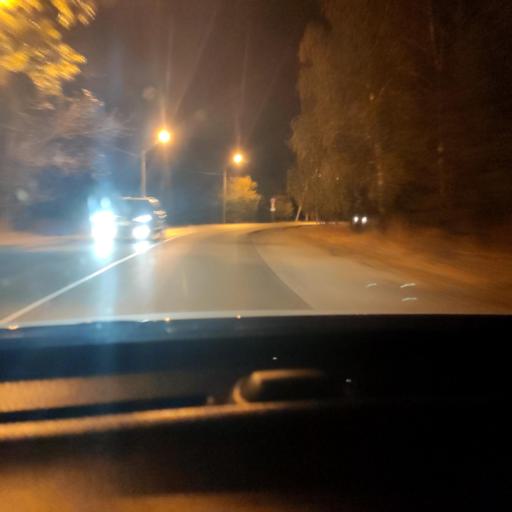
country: RU
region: Voronezj
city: Somovo
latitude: 51.7316
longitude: 39.3200
